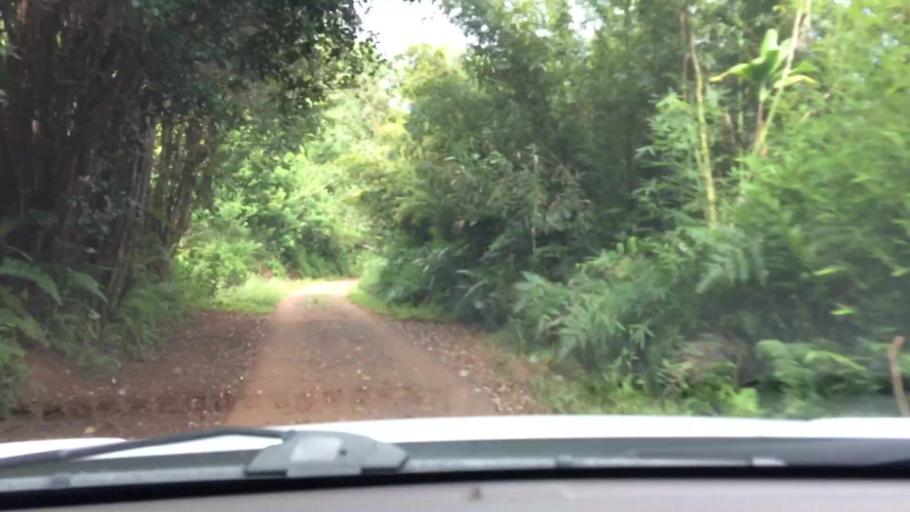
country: US
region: Hawaii
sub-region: Hawaii County
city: Pepeekeo
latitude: 19.8260
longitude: -155.1126
